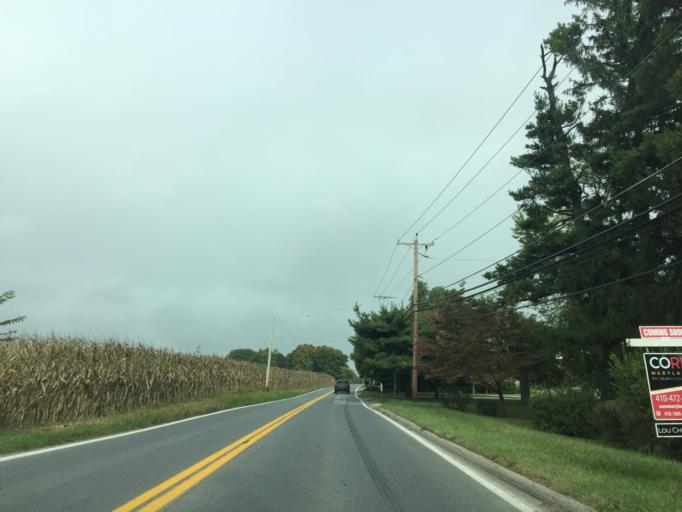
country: US
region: Maryland
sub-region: Baltimore County
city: Garrison
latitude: 39.4495
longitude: -76.7241
